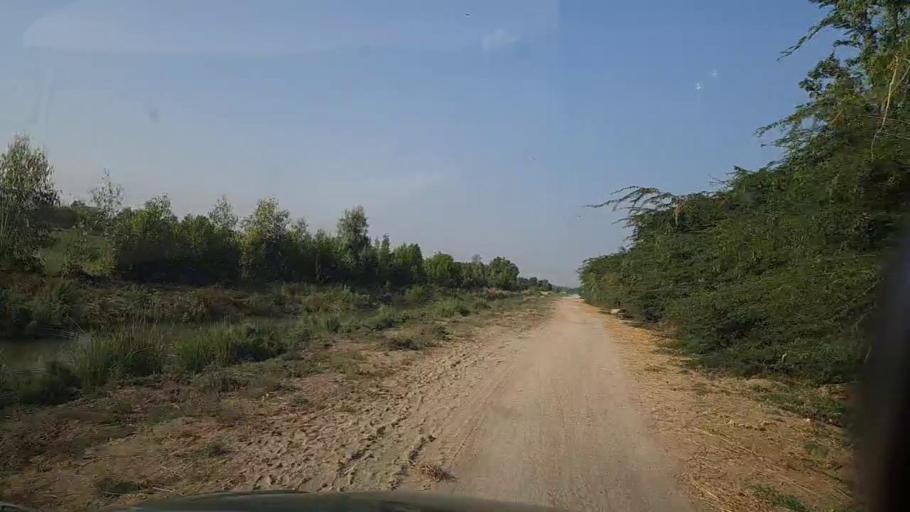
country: PK
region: Sindh
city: Thatta
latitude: 24.6108
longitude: 67.8763
